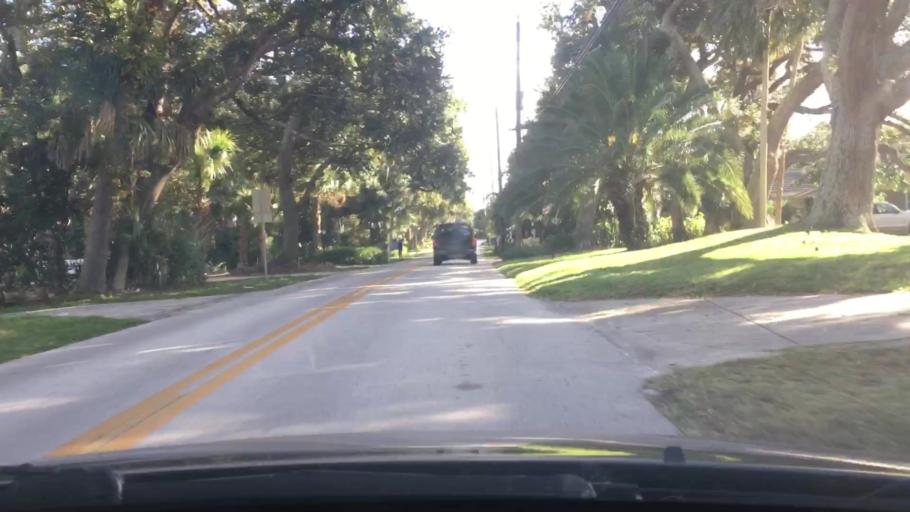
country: US
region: Florida
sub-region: Volusia County
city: Ormond-by-the-Sea
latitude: 29.3439
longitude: -81.0716
